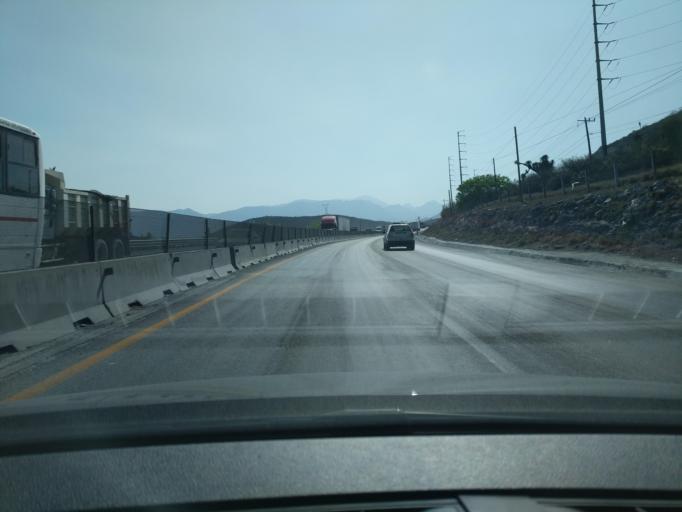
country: MX
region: Nuevo Leon
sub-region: Garcia
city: Los Parques
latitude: 25.7559
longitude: -100.4990
